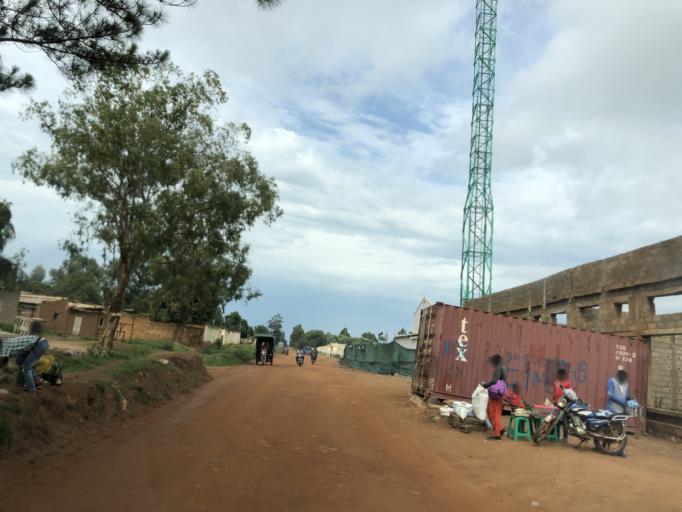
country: AO
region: Cuanza Sul
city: Uacu Cungo
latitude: -11.3481
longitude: 15.1013
